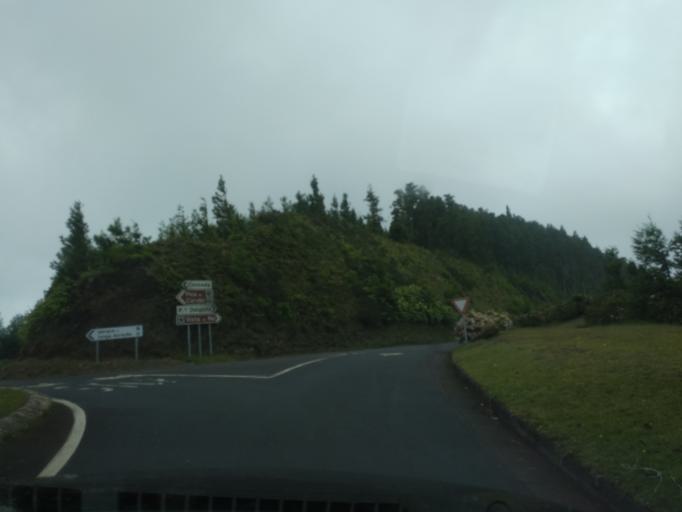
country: PT
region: Azores
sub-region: Ponta Delgada
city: Arrifes
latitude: 37.8369
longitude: -25.7848
